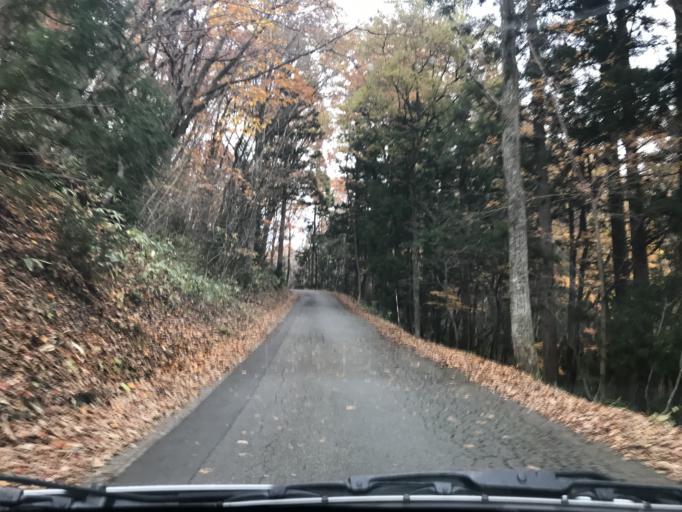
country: JP
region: Iwate
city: Ichinoseki
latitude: 38.9781
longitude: 141.0010
